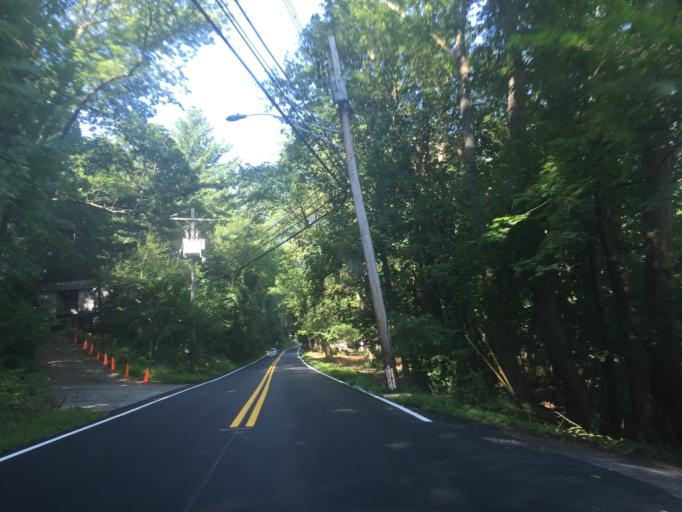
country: US
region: Maryland
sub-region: Baltimore County
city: Pikesville
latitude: 39.4112
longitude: -76.7092
